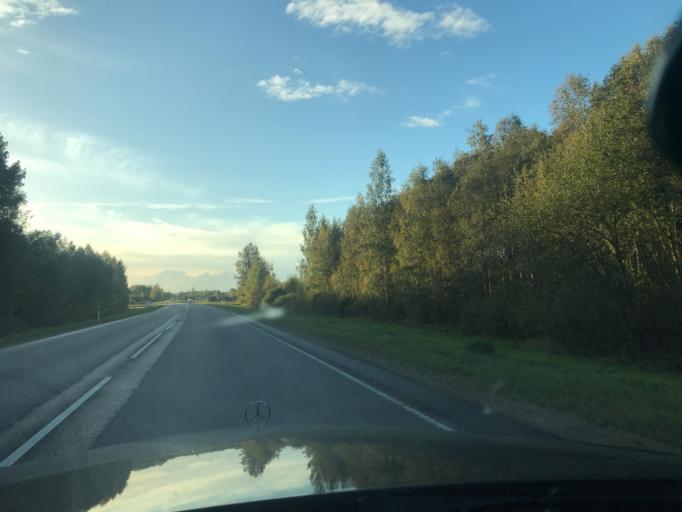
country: EE
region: Vorumaa
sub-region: Voru linn
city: Voru
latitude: 57.8595
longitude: 27.0070
